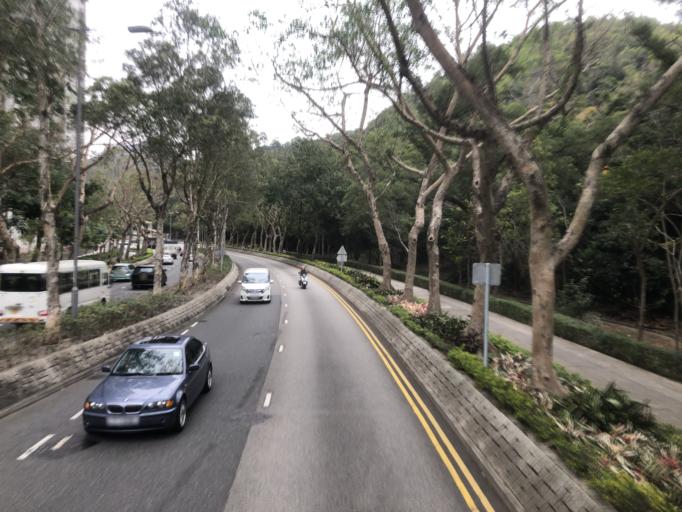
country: HK
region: Sai Kung
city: Sai Kung
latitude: 22.3264
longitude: 114.2581
